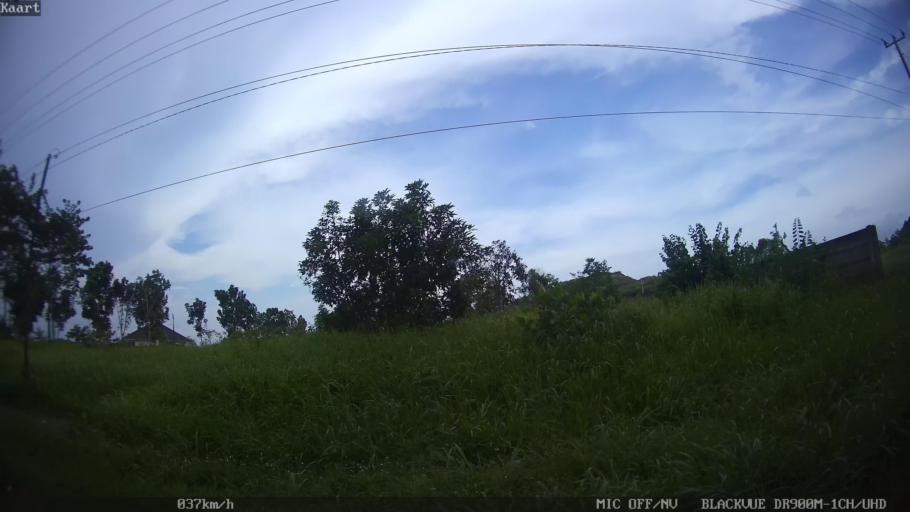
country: ID
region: Lampung
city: Bandarlampung
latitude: -5.4096
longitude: 105.1937
